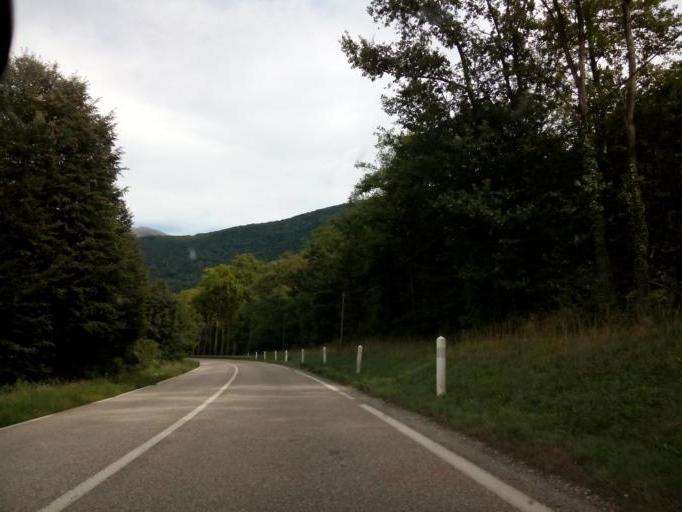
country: FR
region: Rhone-Alpes
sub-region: Departement de l'Isere
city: Notre-Dame-de-Mesage
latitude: 45.0504
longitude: 5.7830
